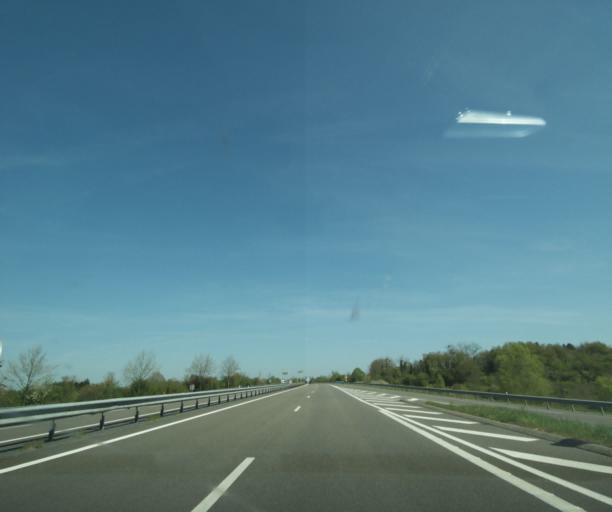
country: FR
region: Bourgogne
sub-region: Departement de la Nievre
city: Saint-Eloi
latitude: 46.9797
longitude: 3.2023
